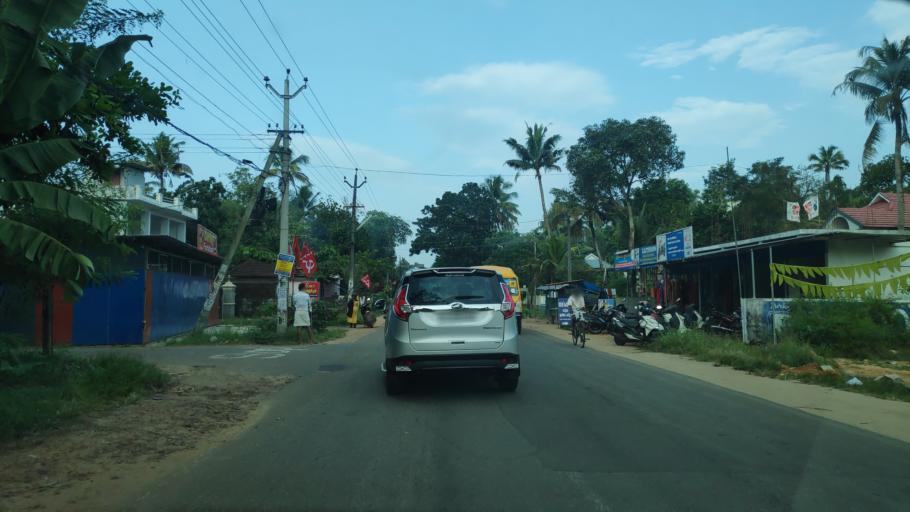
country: IN
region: Kerala
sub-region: Alappuzha
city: Alleppey
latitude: 9.5626
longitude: 76.3455
